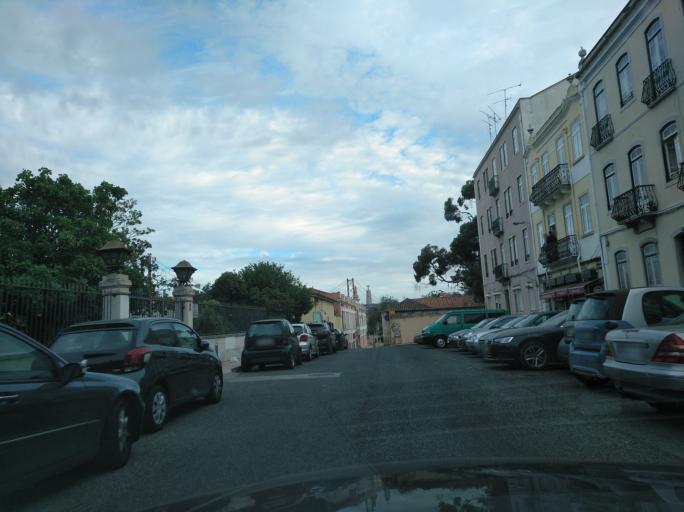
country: PT
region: Setubal
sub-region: Almada
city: Pragal
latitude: 38.6999
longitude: -9.1904
